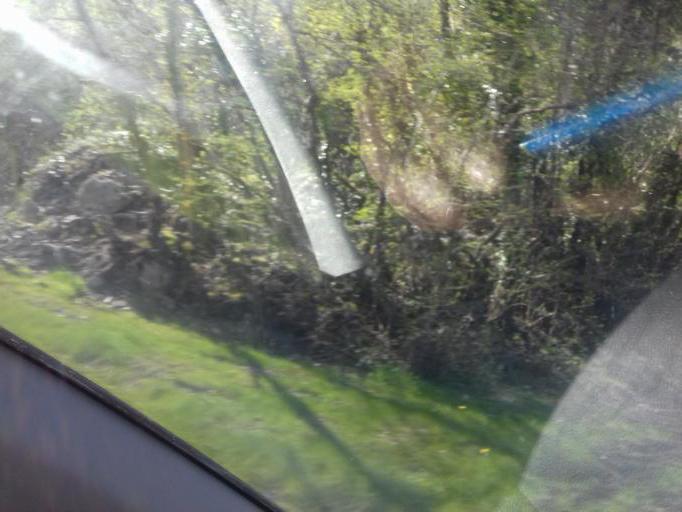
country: GB
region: Northern Ireland
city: Irvinestown
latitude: 54.4179
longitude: -7.7324
